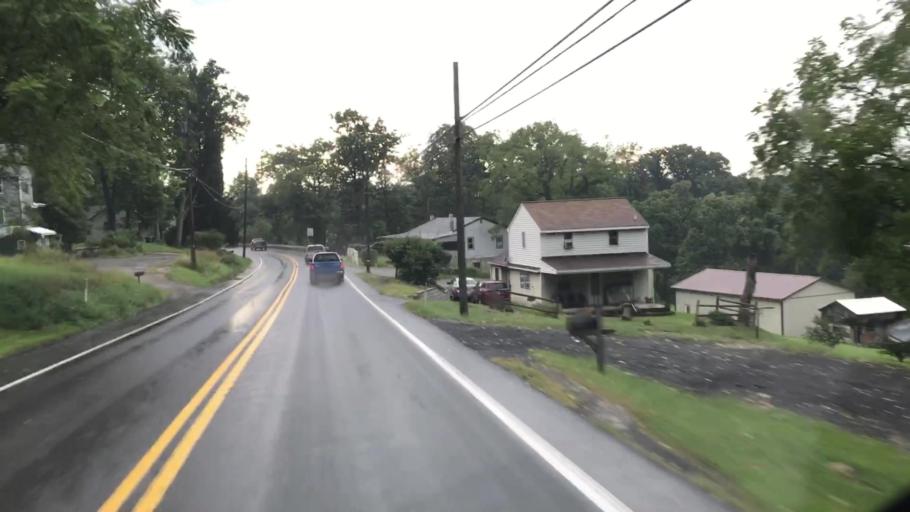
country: US
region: Pennsylvania
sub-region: Cumberland County
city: Schlusser
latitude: 40.2977
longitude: -77.1359
